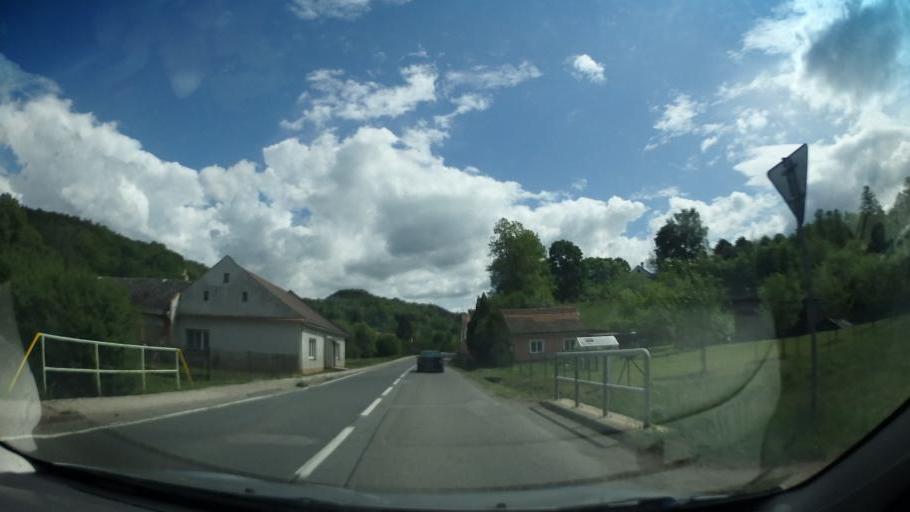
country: CZ
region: Pardubicky
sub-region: Okres Svitavy
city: Moravska Trebova
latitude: 49.7068
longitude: 16.6409
